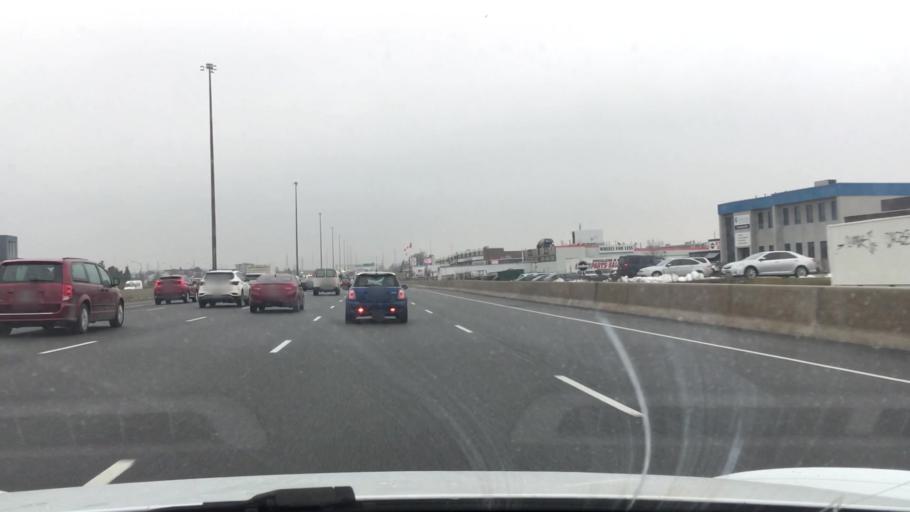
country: CA
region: Ontario
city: Concord
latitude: 43.7411
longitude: -79.5272
